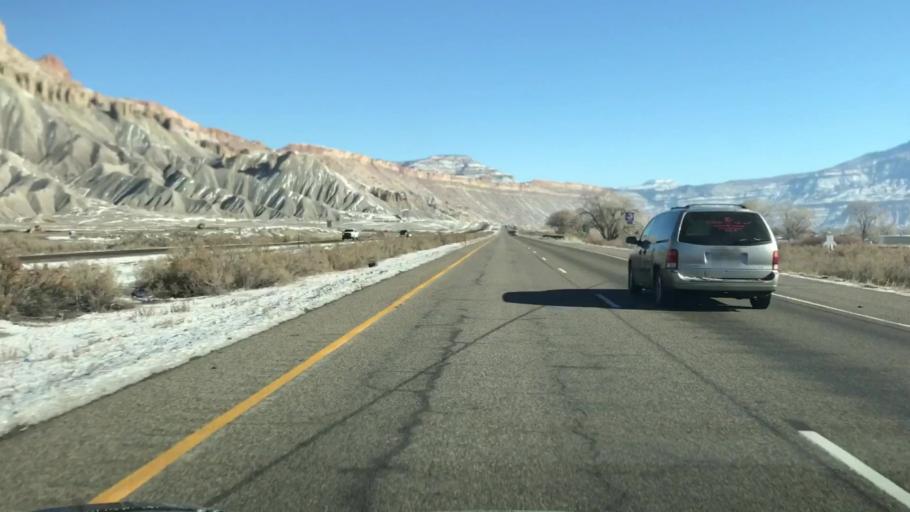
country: US
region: Colorado
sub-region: Mesa County
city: Clifton
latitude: 39.1088
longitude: -108.4245
